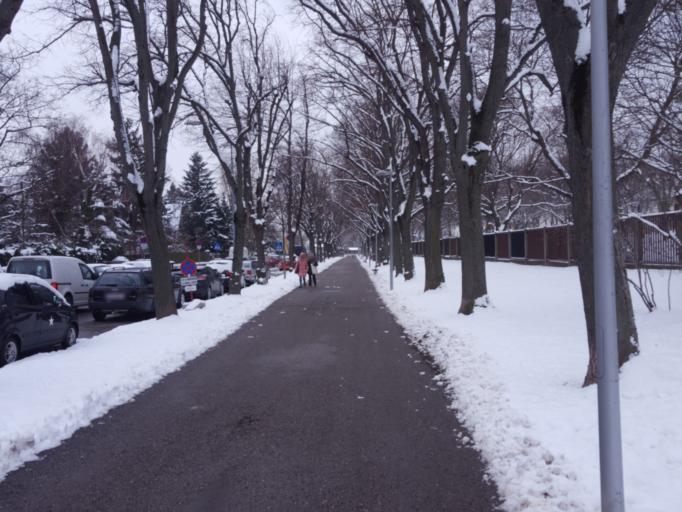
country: AT
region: Lower Austria
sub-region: Politischer Bezirk Modling
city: Vosendorf
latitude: 48.1725
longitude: 16.3103
